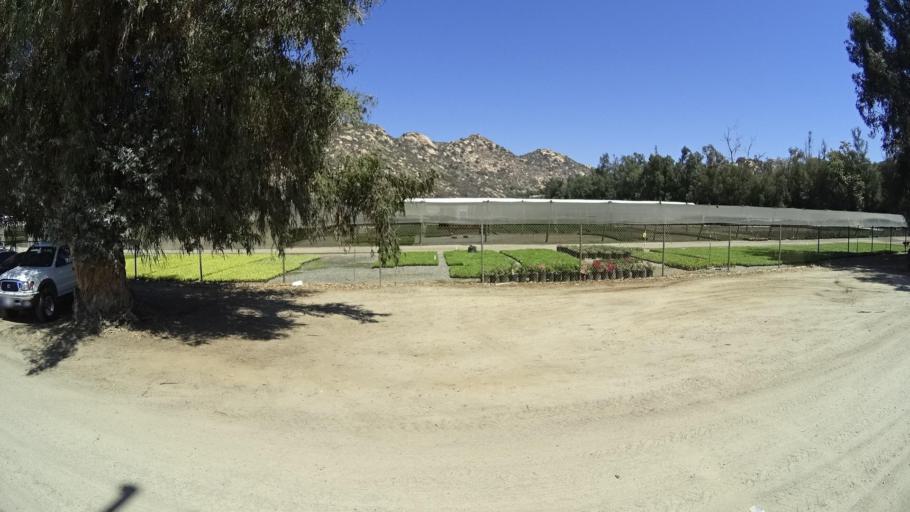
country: US
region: California
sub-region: San Diego County
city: Rainbow
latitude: 33.4212
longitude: -117.1509
